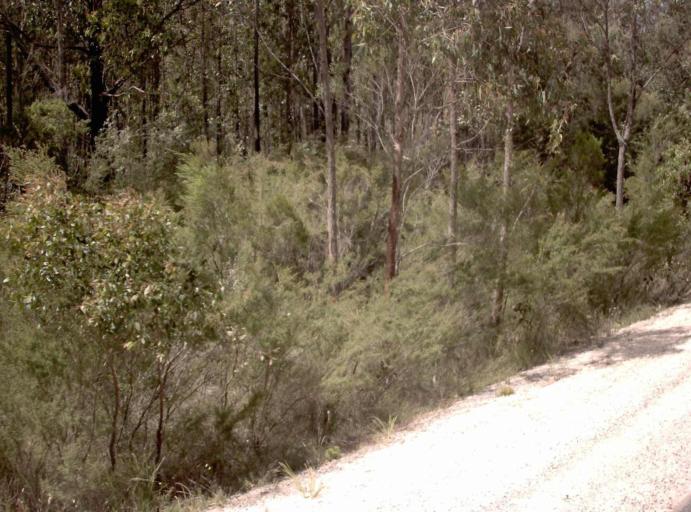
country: AU
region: New South Wales
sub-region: Bombala
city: Bombala
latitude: -37.5460
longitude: 149.4318
